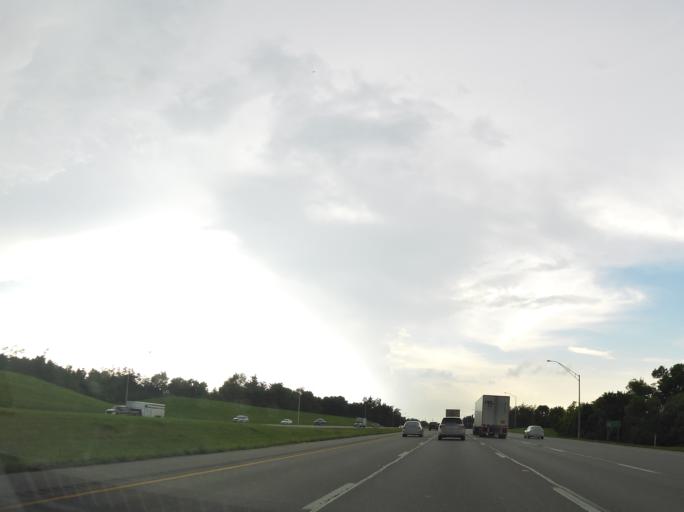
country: US
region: Kentucky
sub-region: Fayette County
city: Lexington-Fayette
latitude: 38.0593
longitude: -84.4348
